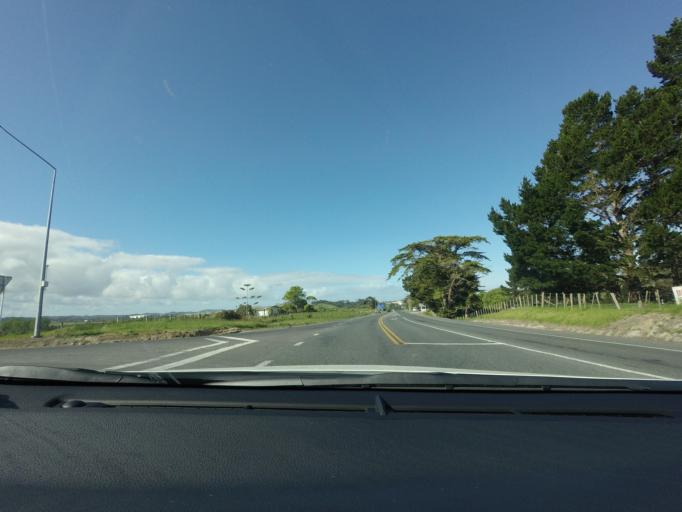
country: NZ
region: Auckland
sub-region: Auckland
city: Rothesay Bay
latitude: -36.6274
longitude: 174.6582
